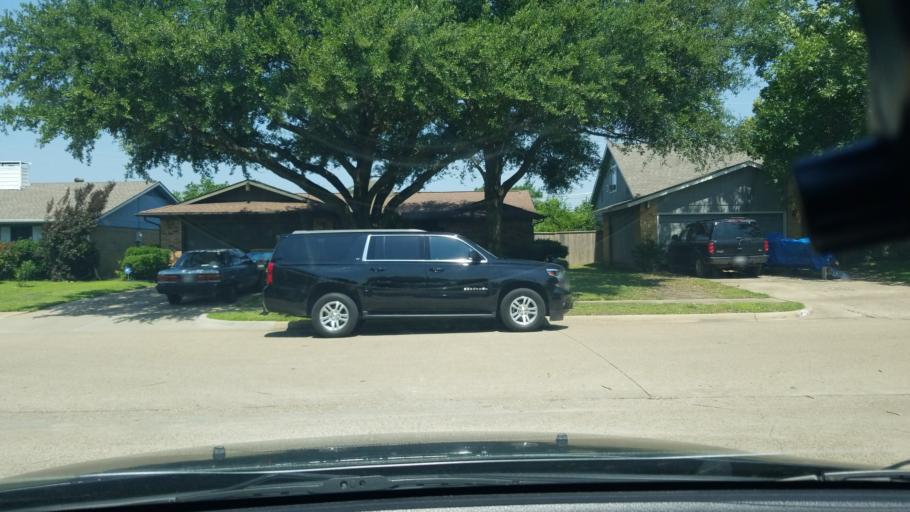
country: US
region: Texas
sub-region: Dallas County
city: Sunnyvale
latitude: 32.8252
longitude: -96.6068
